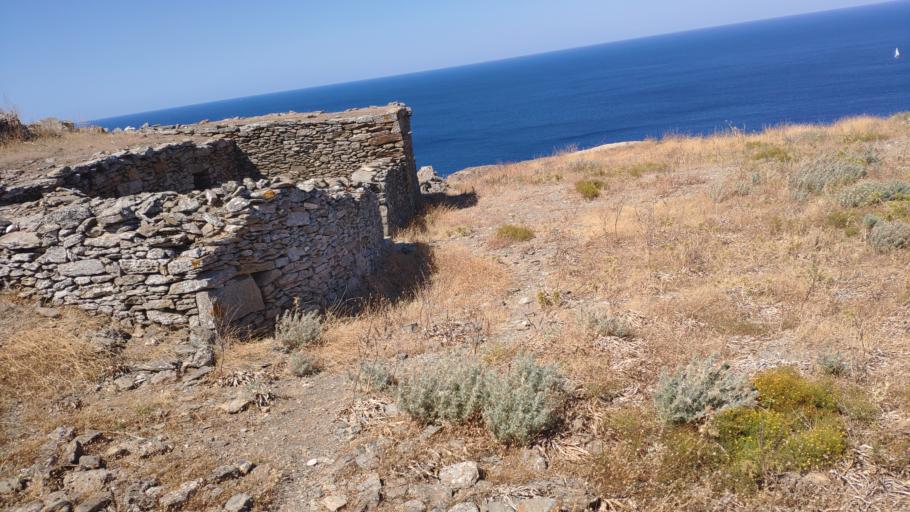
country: GR
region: South Aegean
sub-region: Nomos Kykladon
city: Kythnos
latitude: 37.4072
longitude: 24.3956
